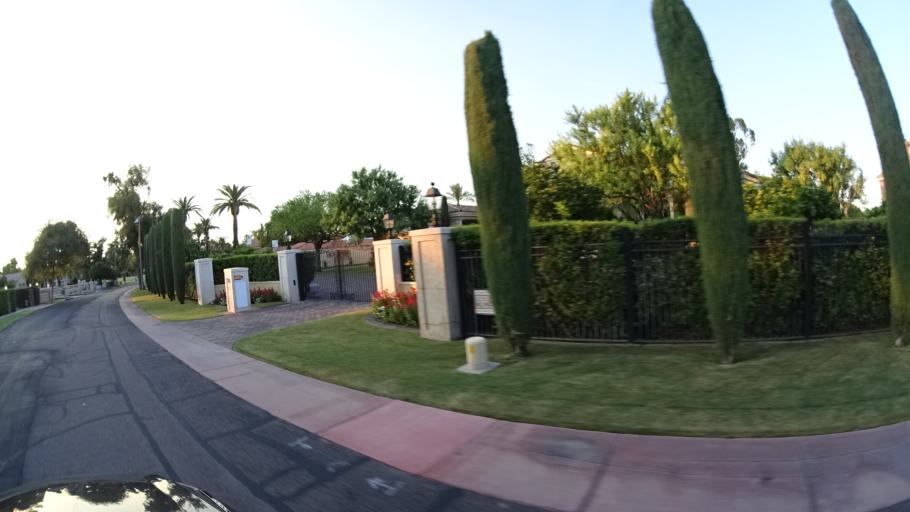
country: US
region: Arizona
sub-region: Maricopa County
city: Phoenix
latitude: 33.5123
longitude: -112.0235
